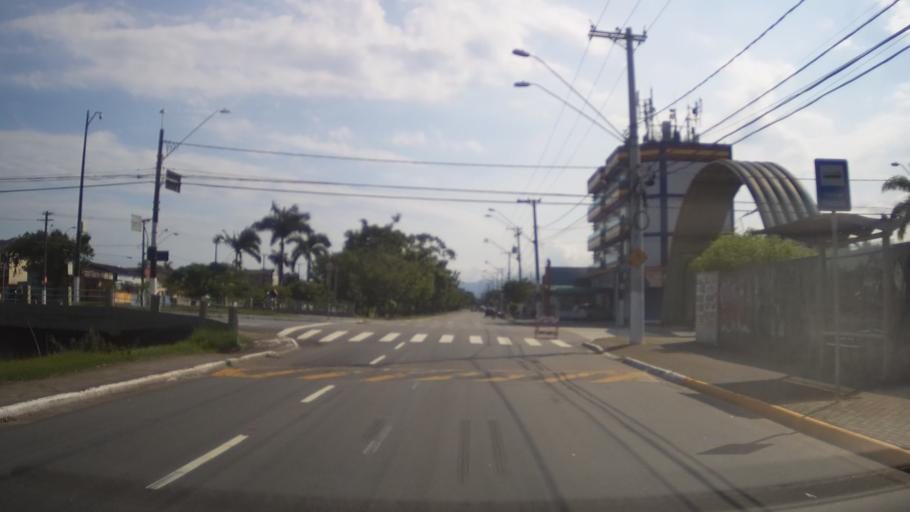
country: BR
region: Sao Paulo
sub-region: Praia Grande
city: Praia Grande
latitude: -24.0001
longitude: -46.4205
